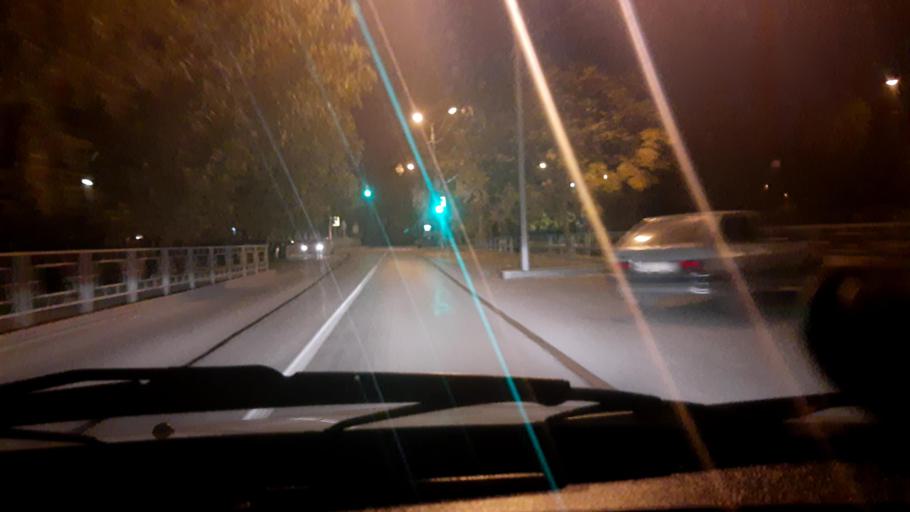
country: RU
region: Bashkortostan
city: Ufa
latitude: 54.7209
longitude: 56.0127
